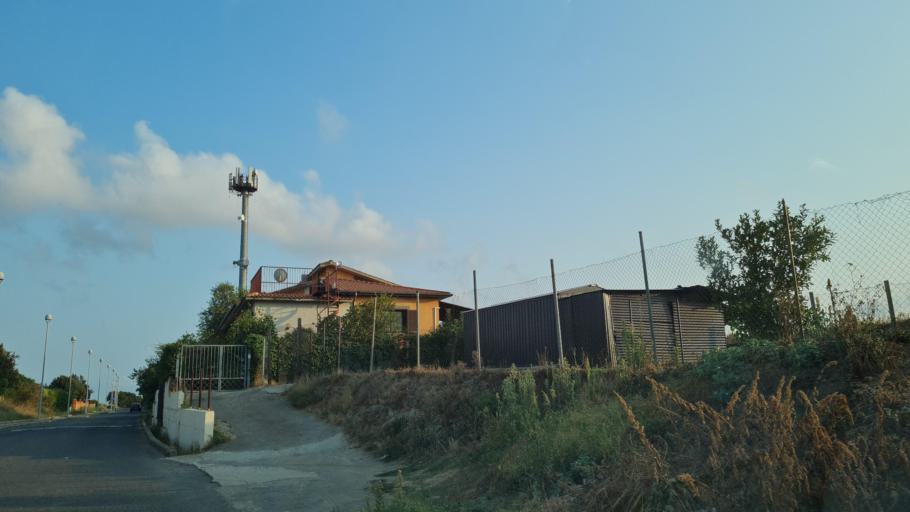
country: IT
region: Latium
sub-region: Provincia di Viterbo
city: Montalto di Castro
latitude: 42.3454
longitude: 11.6094
